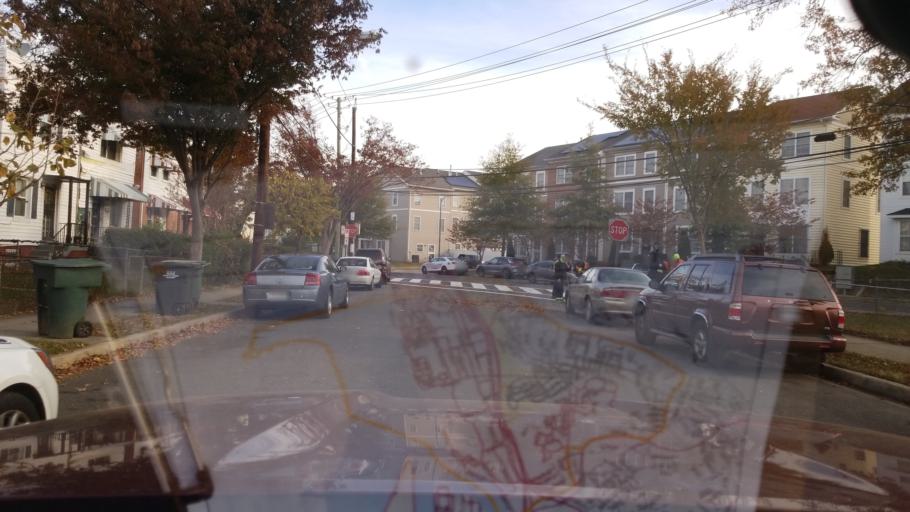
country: US
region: Maryland
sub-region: Prince George's County
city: Hillcrest Heights
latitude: 38.8476
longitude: -76.9831
